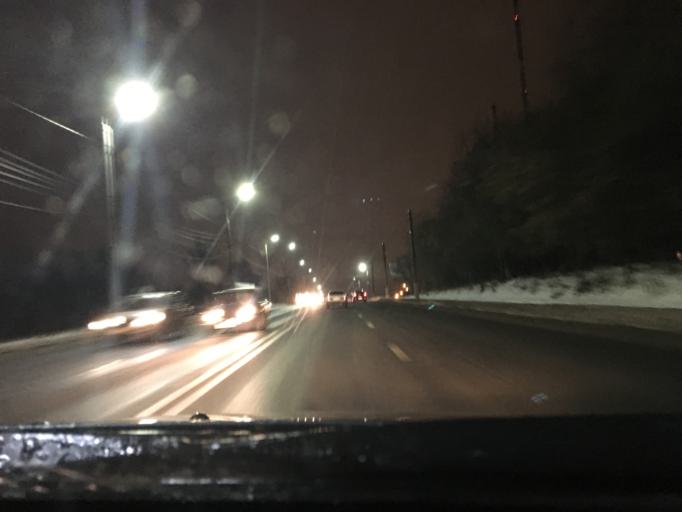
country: RU
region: Tula
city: Mendeleyevskiy
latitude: 54.1368
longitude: 37.5800
